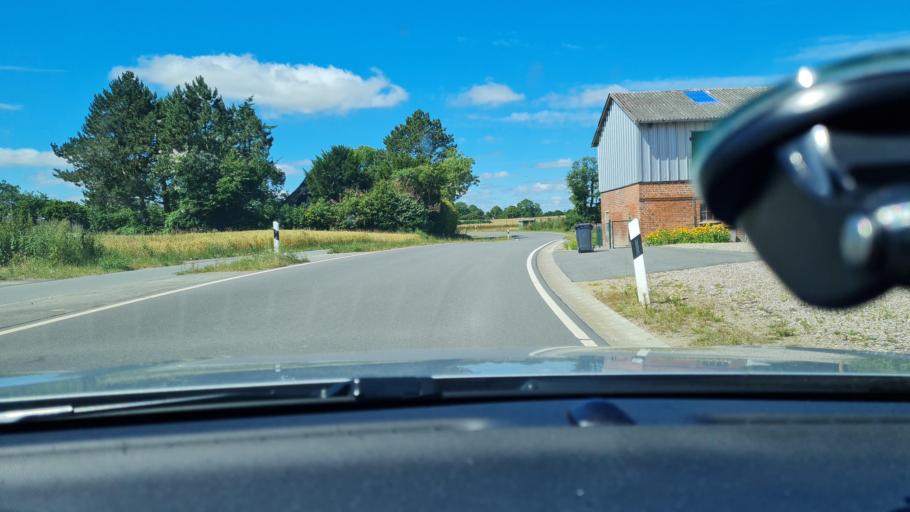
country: DE
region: Schleswig-Holstein
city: Kronsgaard
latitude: 54.7272
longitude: 9.9584
